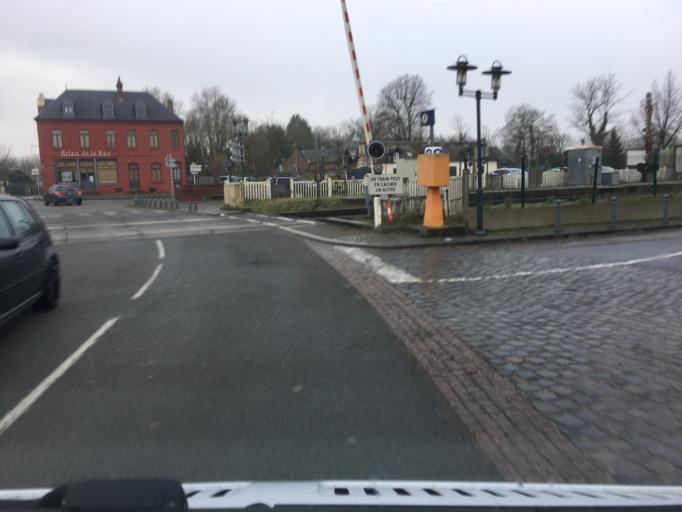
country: FR
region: Picardie
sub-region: Departement de la Somme
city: Sailly-Flibeaucourt
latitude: 50.1867
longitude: 1.7050
